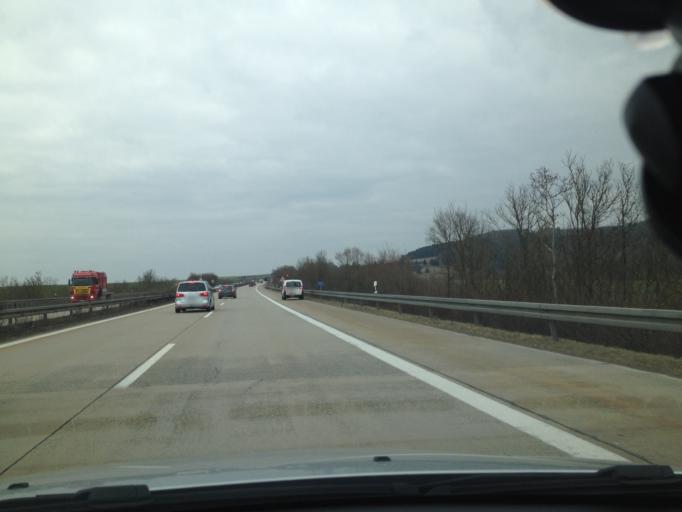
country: DE
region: Bavaria
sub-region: Regierungsbezirk Mittelfranken
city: Diebach
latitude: 49.2980
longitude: 10.2137
